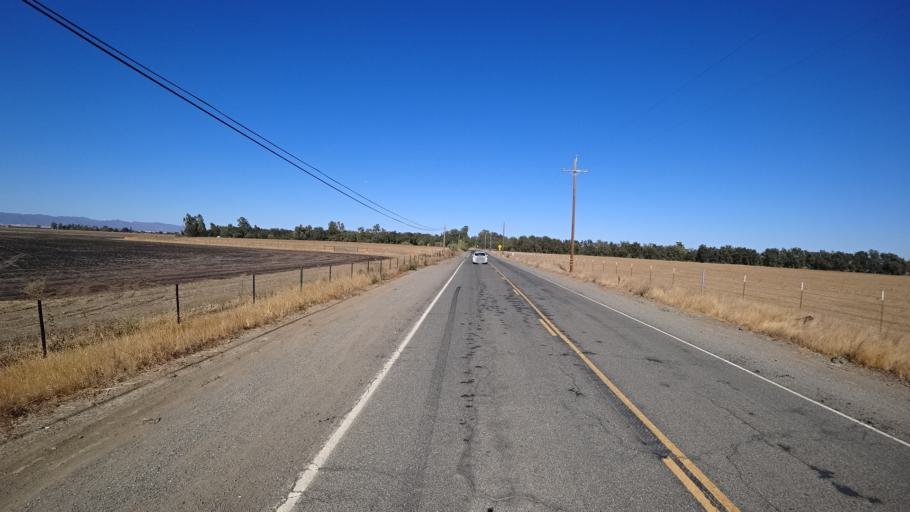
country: US
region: California
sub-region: Solano County
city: Dixon
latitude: 38.5431
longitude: -121.8538
